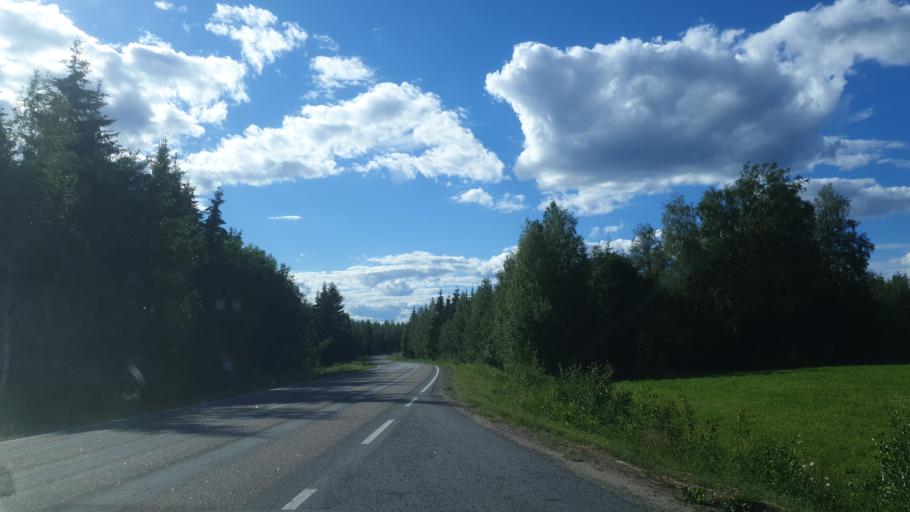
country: FI
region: Southern Savonia
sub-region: Mikkeli
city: Maentyharju
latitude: 61.4827
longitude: 26.7415
